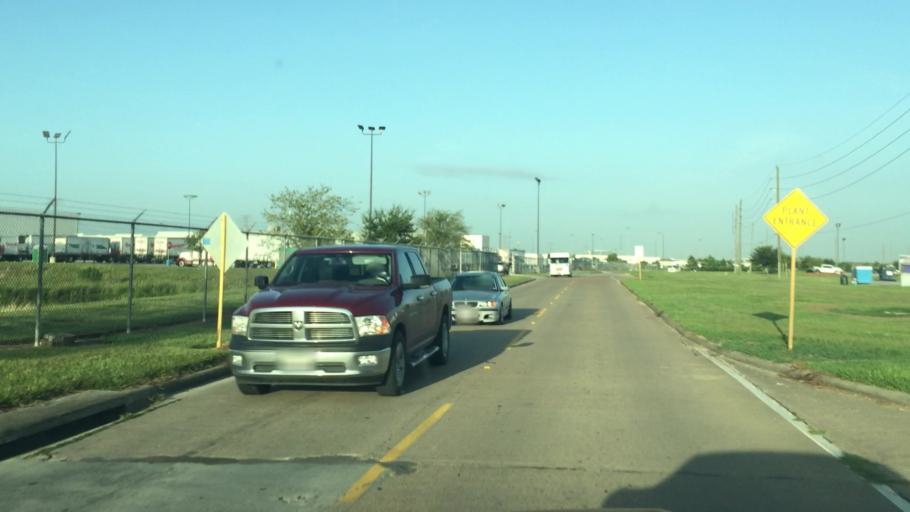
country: US
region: Texas
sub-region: Harris County
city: Hudson
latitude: 29.9428
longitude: -95.4845
